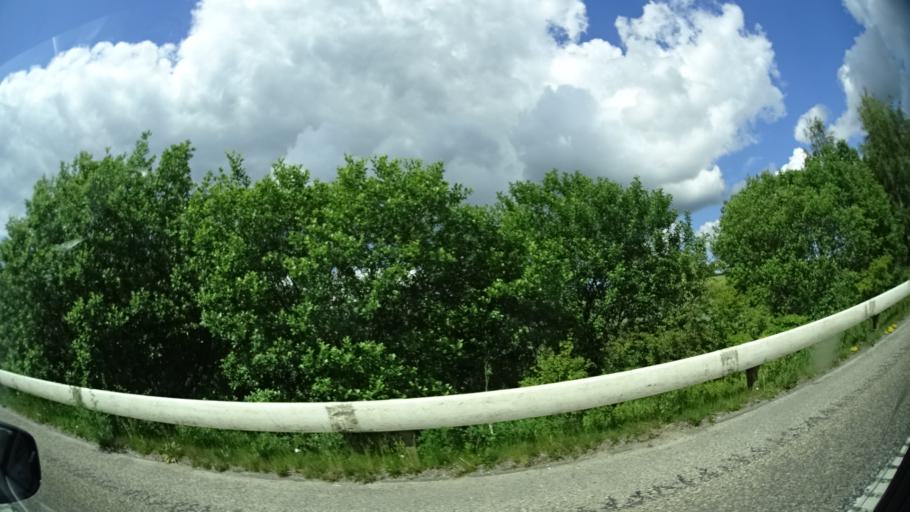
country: DK
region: Central Jutland
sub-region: Syddjurs Kommune
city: Ronde
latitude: 56.3167
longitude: 10.4433
